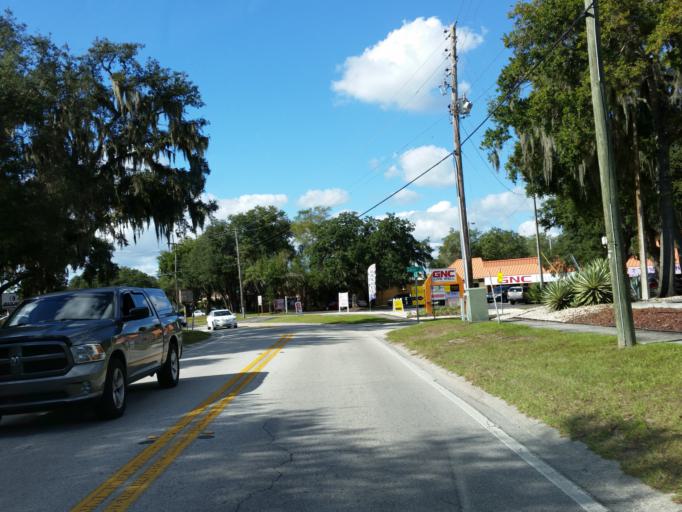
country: US
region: Florida
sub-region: Hillsborough County
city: Brandon
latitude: 27.9338
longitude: -82.2918
